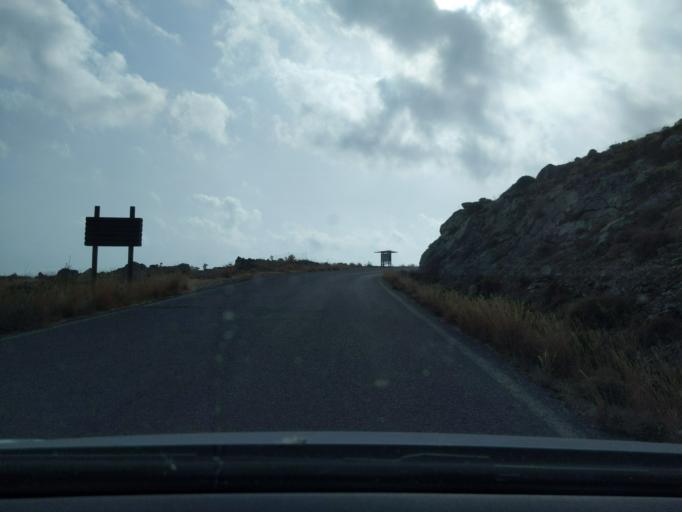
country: GR
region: Crete
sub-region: Nomos Lasithiou
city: Palekastro
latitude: 35.0935
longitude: 26.2623
